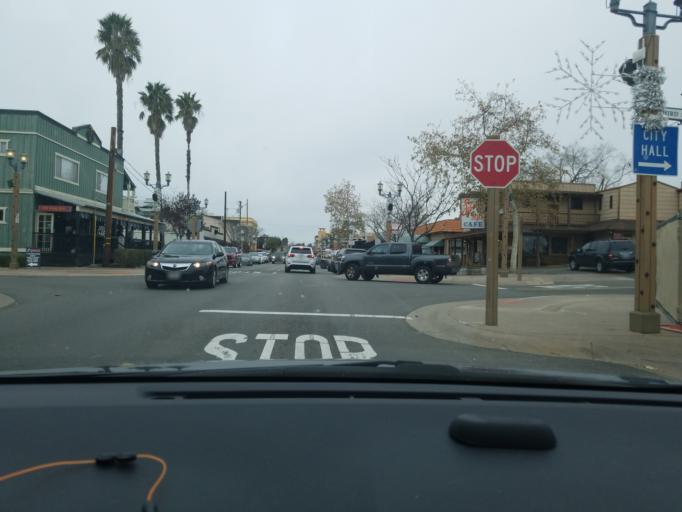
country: US
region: California
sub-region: Riverside County
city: Temecula
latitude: 33.4926
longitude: -117.1478
